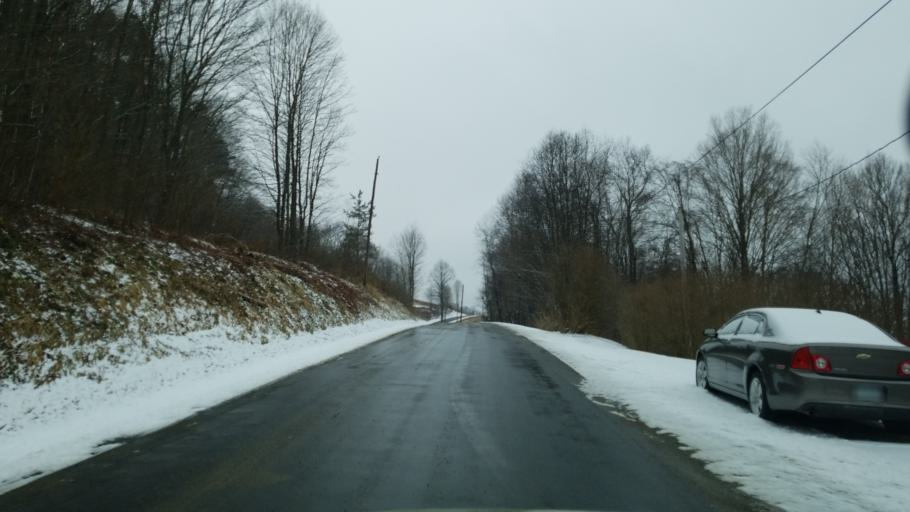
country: US
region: Pennsylvania
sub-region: Jefferson County
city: Sykesville
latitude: 41.0841
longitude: -78.8285
